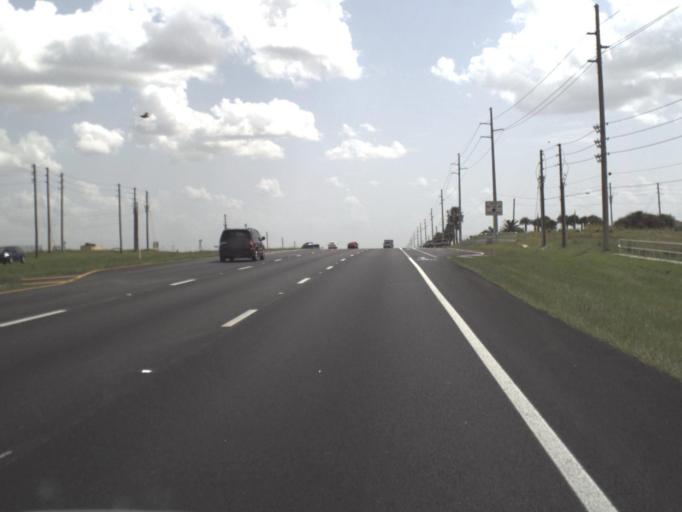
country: US
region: Florida
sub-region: Lake County
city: Four Corners
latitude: 28.2758
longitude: -81.6622
